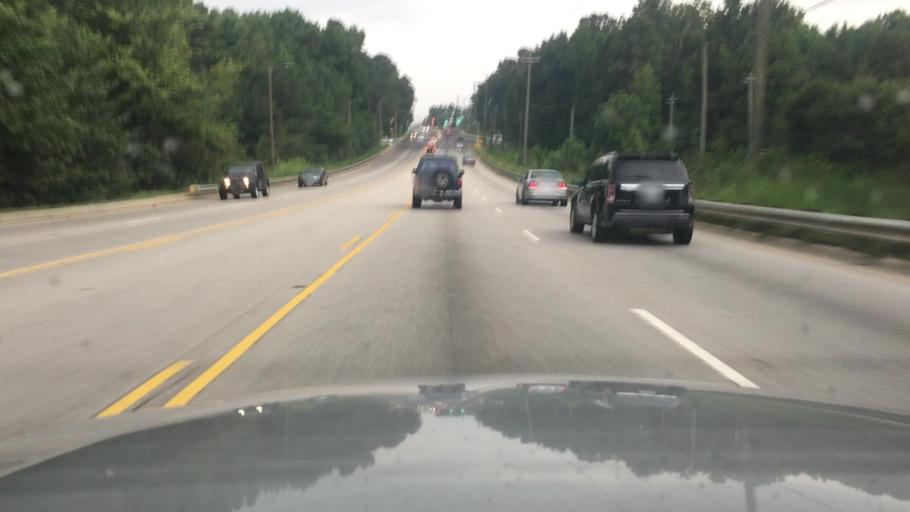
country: US
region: North Carolina
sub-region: Cumberland County
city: Fort Bragg
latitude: 35.0743
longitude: -79.0113
